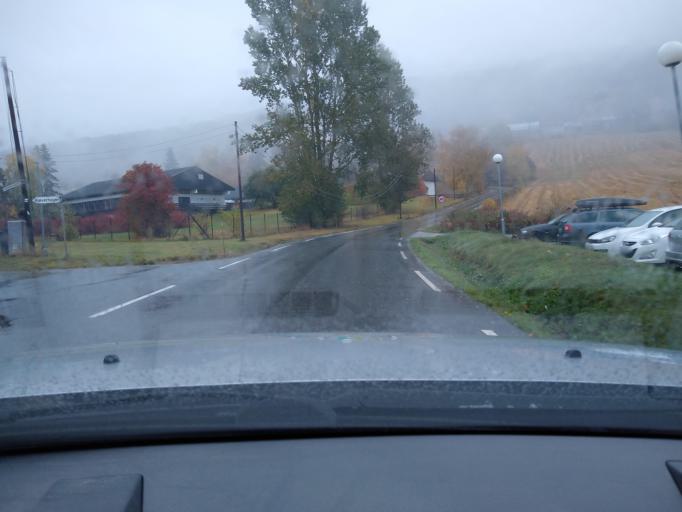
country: NO
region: Oppland
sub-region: Ringebu
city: Ringebu
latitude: 61.5347
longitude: 10.1455
